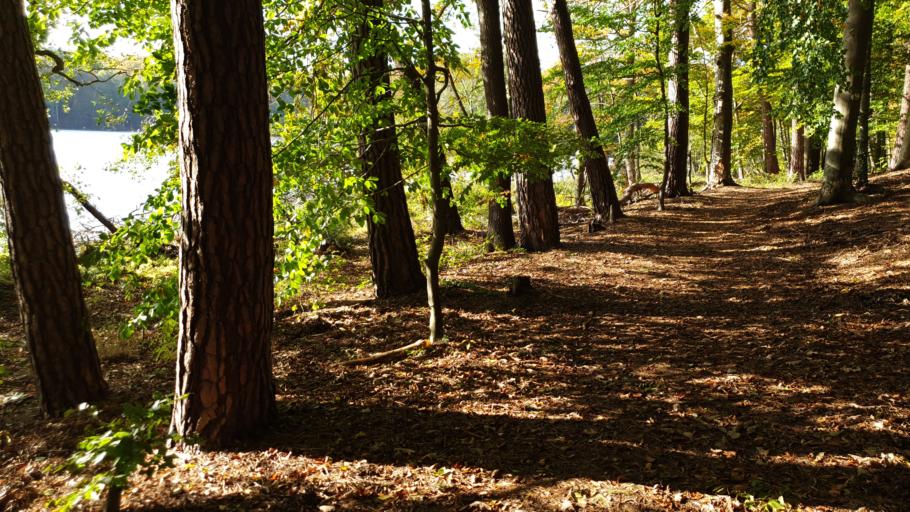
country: DE
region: Brandenburg
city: Liepe
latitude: 52.8783
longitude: 13.9667
